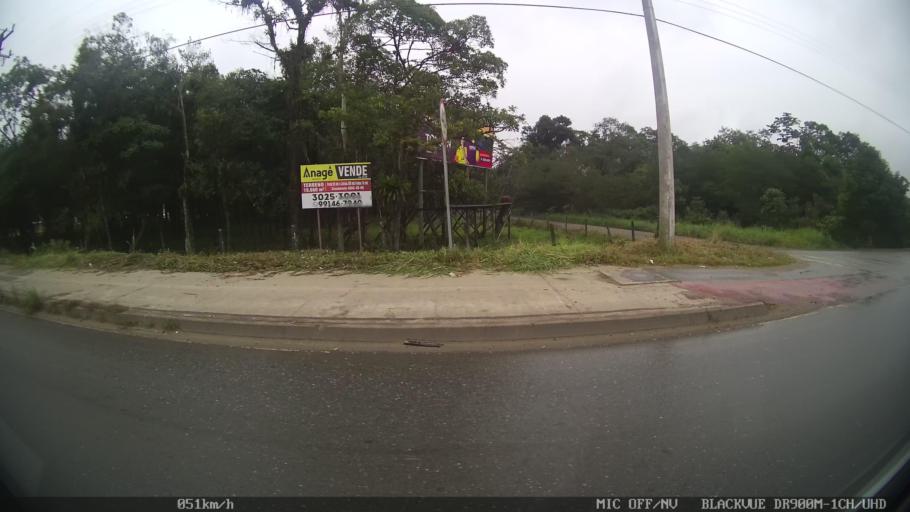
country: BR
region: Santa Catarina
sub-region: Joinville
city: Joinville
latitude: -26.2296
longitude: -48.8062
